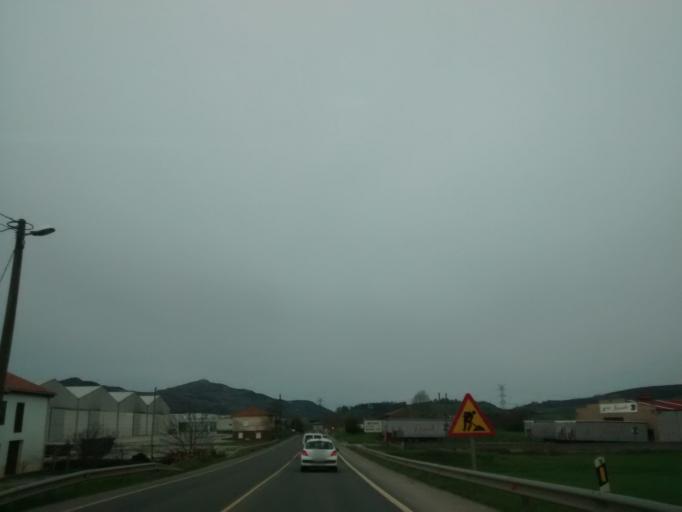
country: ES
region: Cantabria
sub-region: Provincia de Cantabria
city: Santa Maria de Cayon
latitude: 43.3331
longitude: -3.8375
